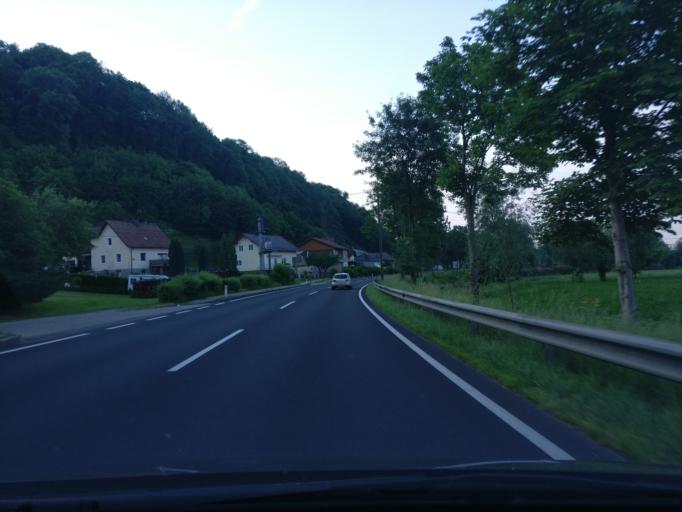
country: AT
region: Upper Austria
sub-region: Politischer Bezirk Urfahr-Umgebung
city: Steyregg
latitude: 48.2937
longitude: 14.3444
